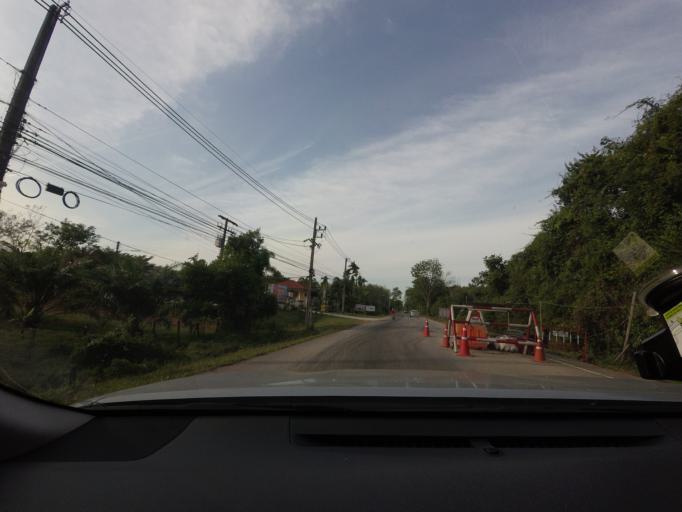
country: TH
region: Narathiwat
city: Ra-ngae
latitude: 6.3127
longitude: 101.7280
